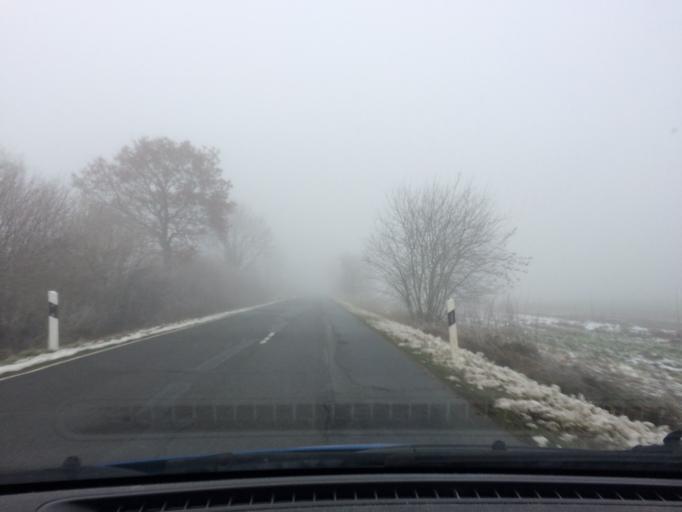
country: DE
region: Schleswig-Holstein
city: Krukow
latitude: 53.4341
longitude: 10.4891
